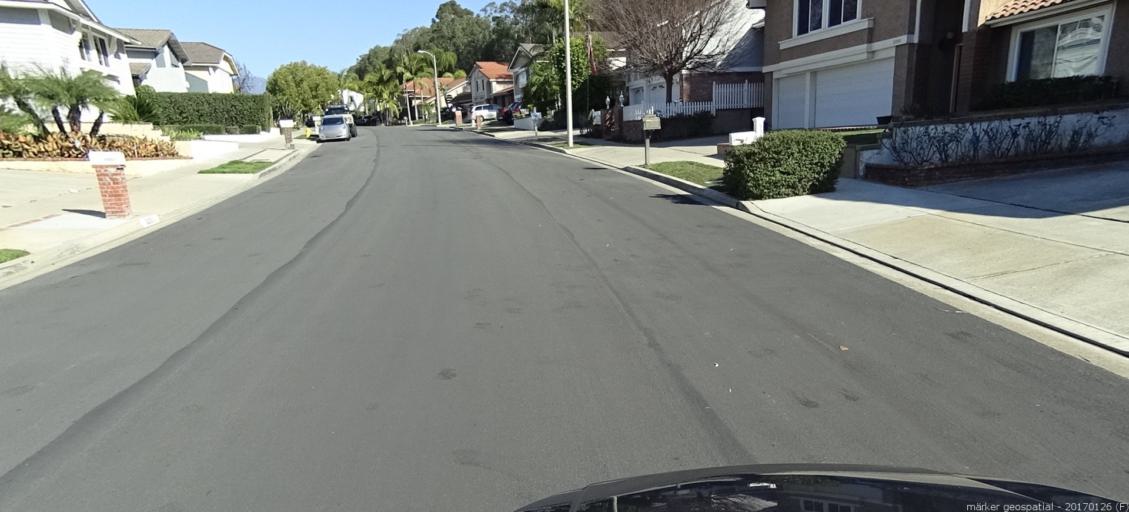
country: US
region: California
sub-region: Orange County
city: Lake Forest
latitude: 33.6396
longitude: -117.7016
